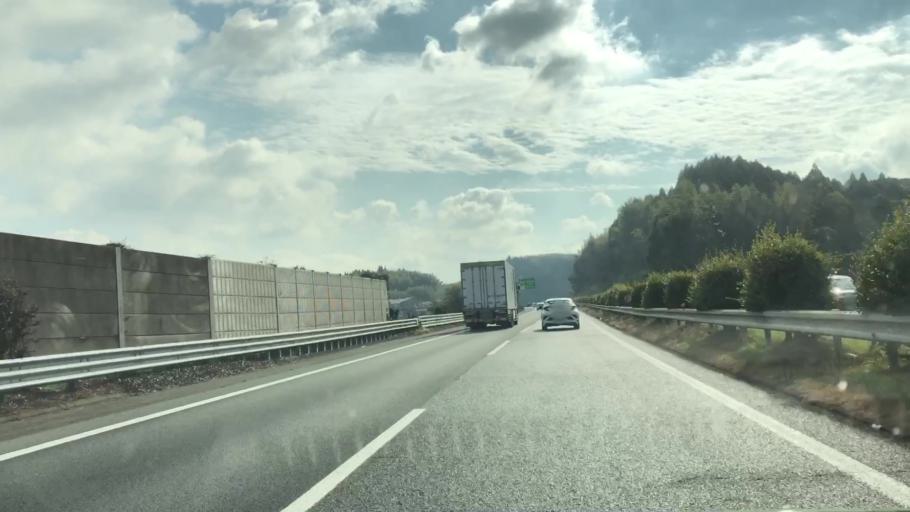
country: JP
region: Fukuoka
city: Setakamachi-takayanagi
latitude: 33.0832
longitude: 130.5417
